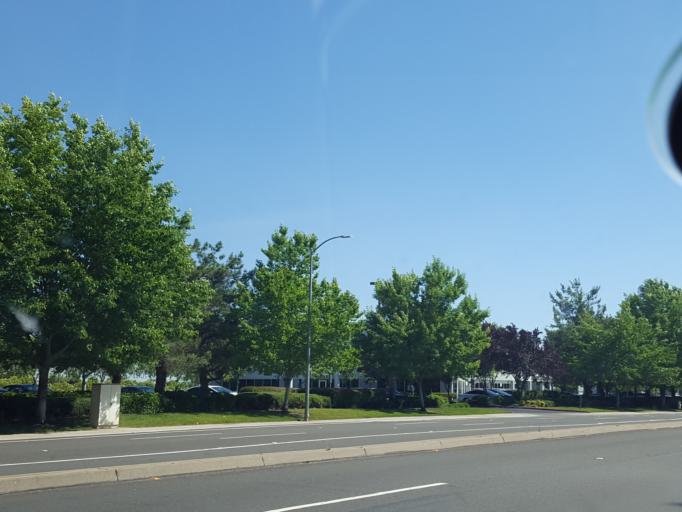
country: US
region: California
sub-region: Sacramento County
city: Rancho Cordova
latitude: 38.5780
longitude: -121.2902
